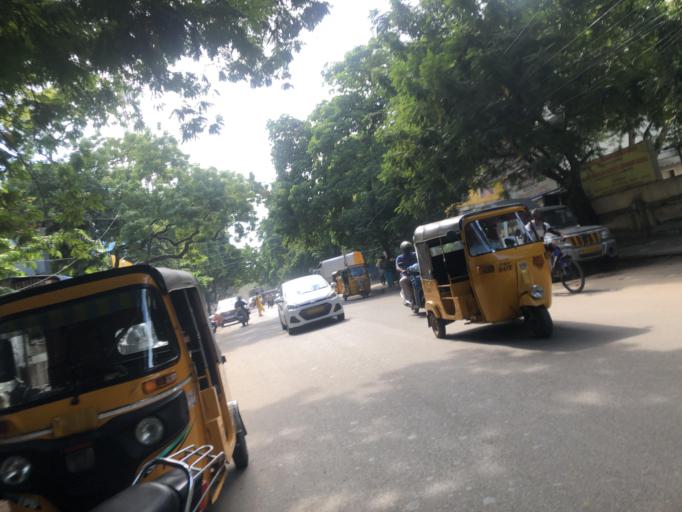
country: IN
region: Tamil Nadu
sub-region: Chennai
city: Gandhi Nagar
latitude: 13.0374
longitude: 80.2627
